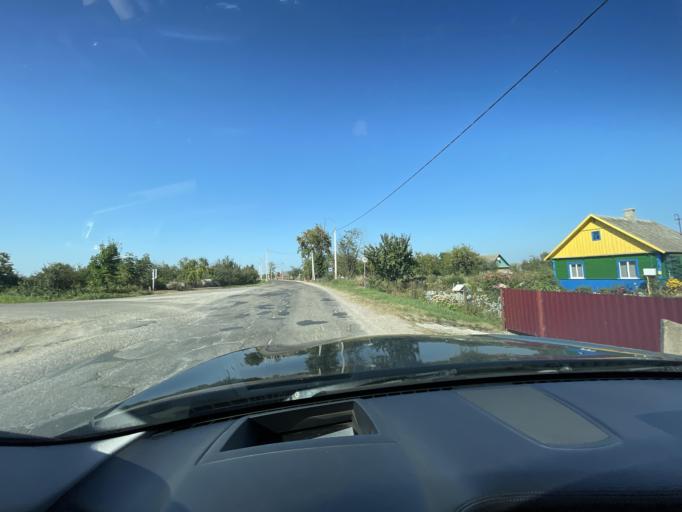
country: BY
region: Grodnenskaya
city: Hrodna
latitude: 53.7258
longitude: 23.9877
